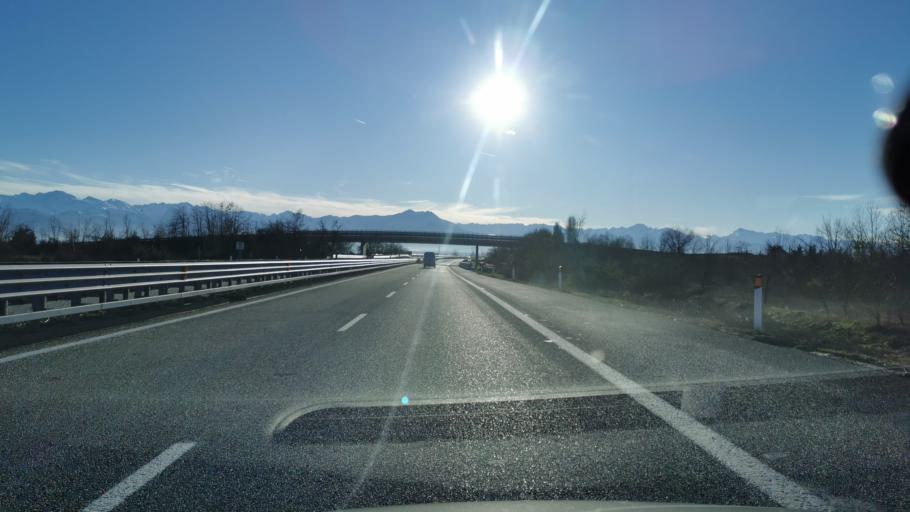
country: IT
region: Piedmont
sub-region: Provincia di Cuneo
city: Magliano Alpi
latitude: 44.4774
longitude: 7.7924
